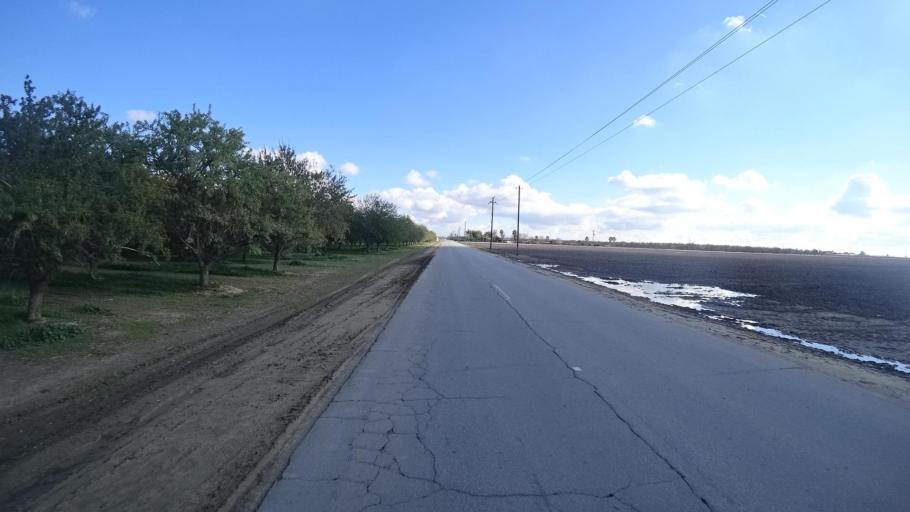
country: US
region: California
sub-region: Kern County
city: McFarland
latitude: 35.6744
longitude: -119.2618
